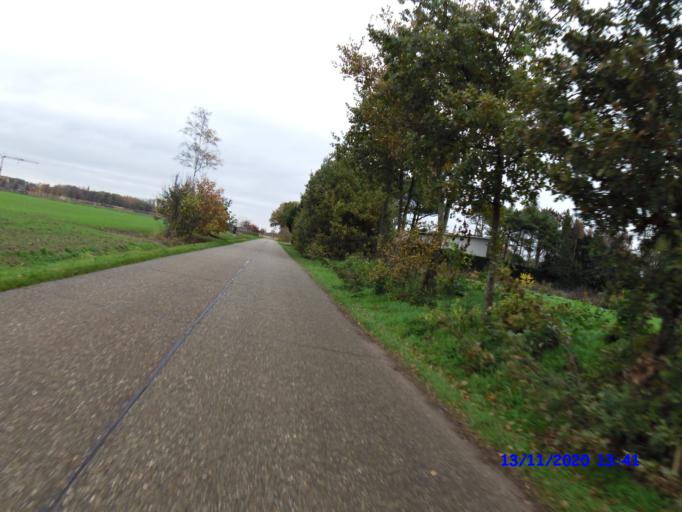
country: BE
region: Flanders
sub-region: Provincie Antwerpen
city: Kasterlee
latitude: 51.2556
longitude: 4.9889
